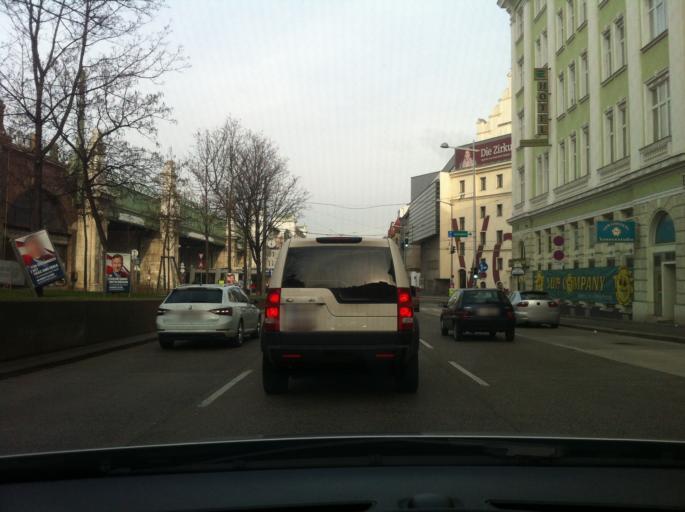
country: AT
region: Vienna
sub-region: Wien Stadt
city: Vienna
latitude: 48.2240
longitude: 16.3495
